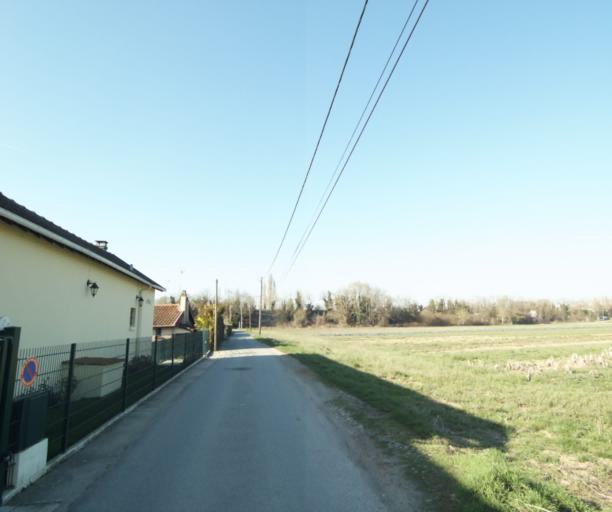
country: FR
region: Ile-de-France
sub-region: Departement du Val-d'Oise
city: Neuville-sur-Oise
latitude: 49.0260
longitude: 2.0656
